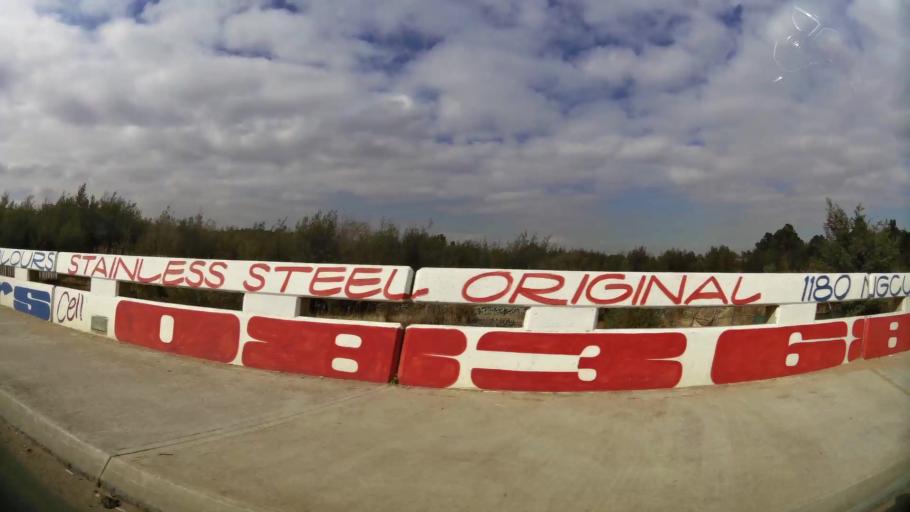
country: ZA
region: Gauteng
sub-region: City of Johannesburg Metropolitan Municipality
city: Roodepoort
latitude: -26.1930
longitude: 27.9055
